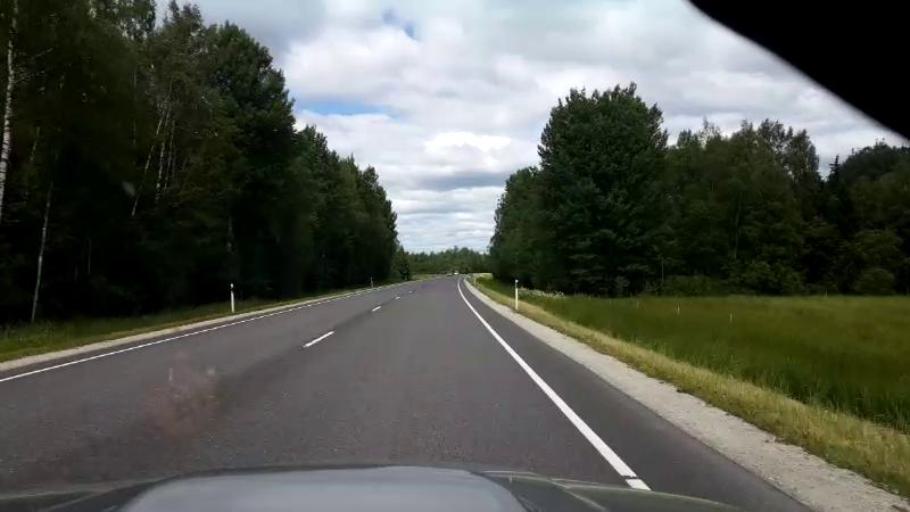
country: EE
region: Raplamaa
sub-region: Maerjamaa vald
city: Marjamaa
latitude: 58.8182
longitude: 24.4127
